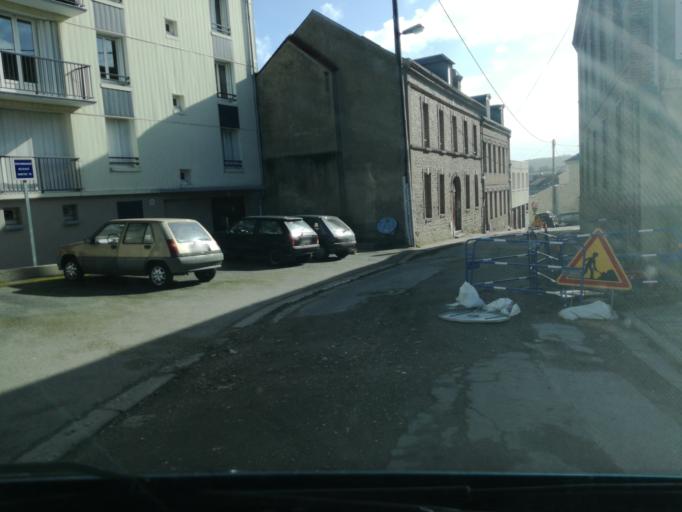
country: FR
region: Haute-Normandie
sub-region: Departement de la Seine-Maritime
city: Fecamp
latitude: 49.7578
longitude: 0.3801
